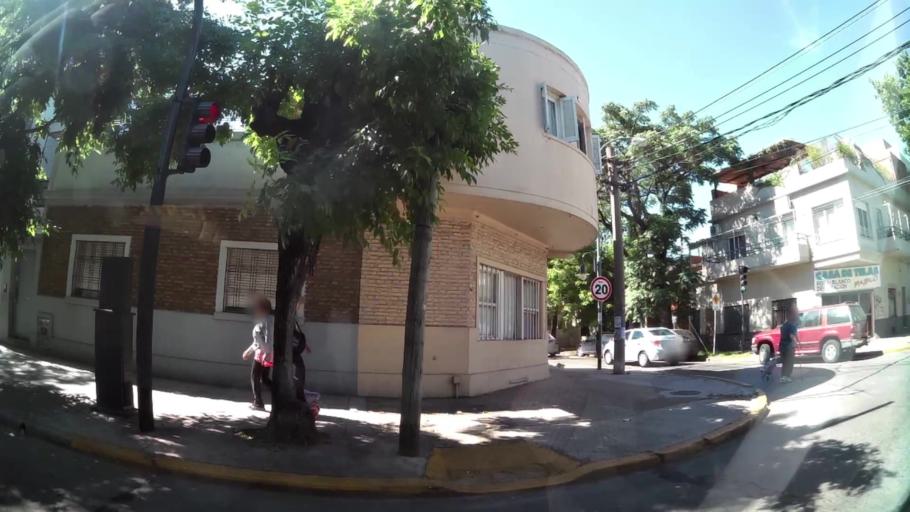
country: AR
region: Buenos Aires
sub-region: Partido de Vicente Lopez
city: Olivos
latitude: -34.5366
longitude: -58.4801
